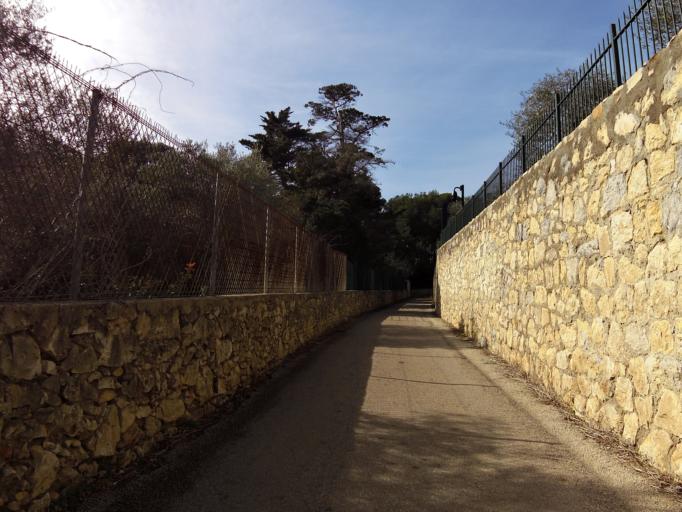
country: FR
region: Provence-Alpes-Cote d'Azur
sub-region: Departement des Alpes-Maritimes
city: Antibes
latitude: 43.5474
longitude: 7.1322
